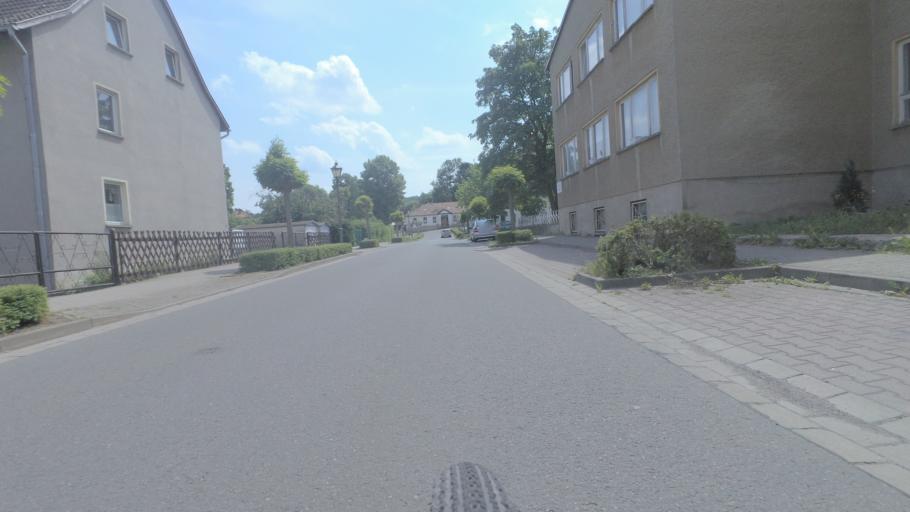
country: DE
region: Saxony-Anhalt
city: Ballenstedt
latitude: 51.7177
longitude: 11.2218
